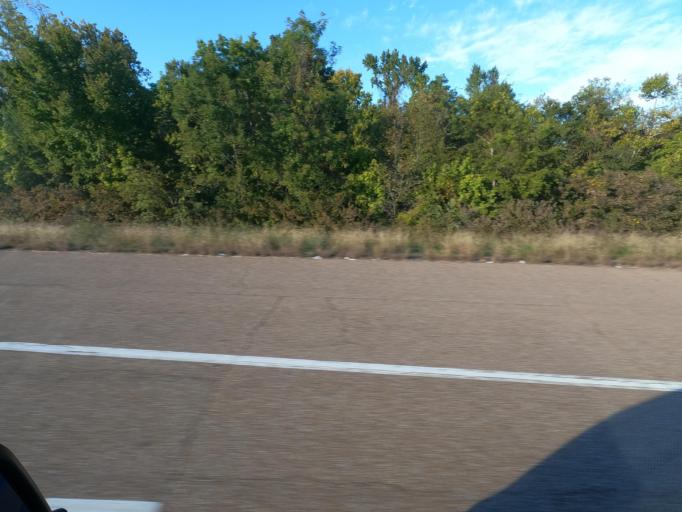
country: US
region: Tennessee
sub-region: Shelby County
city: Millington
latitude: 35.3303
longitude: -89.8934
